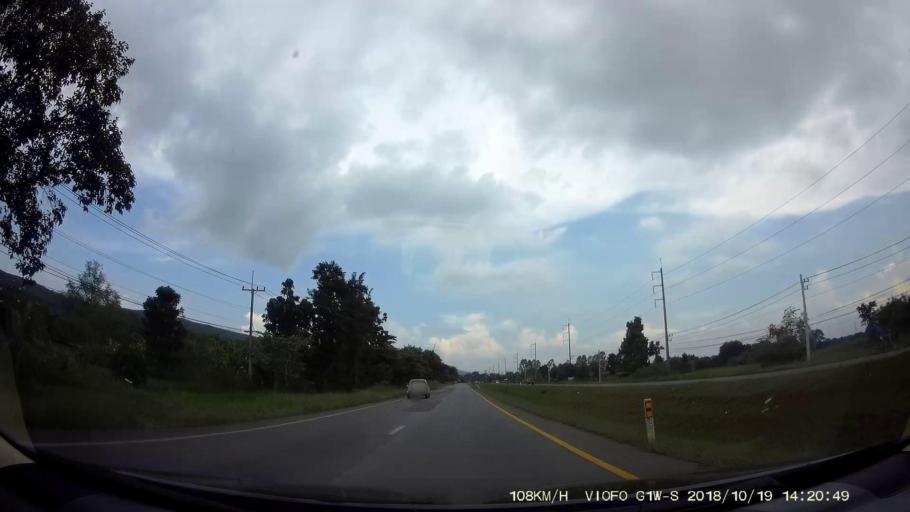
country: TH
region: Chaiyaphum
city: Kaeng Khro
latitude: 16.0451
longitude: 102.2598
